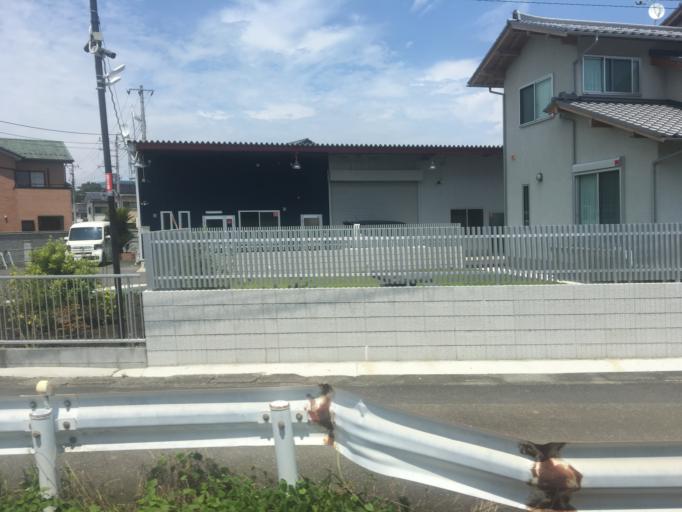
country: JP
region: Saitama
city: Kodamacho-kodamaminami
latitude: 36.1888
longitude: 139.1401
